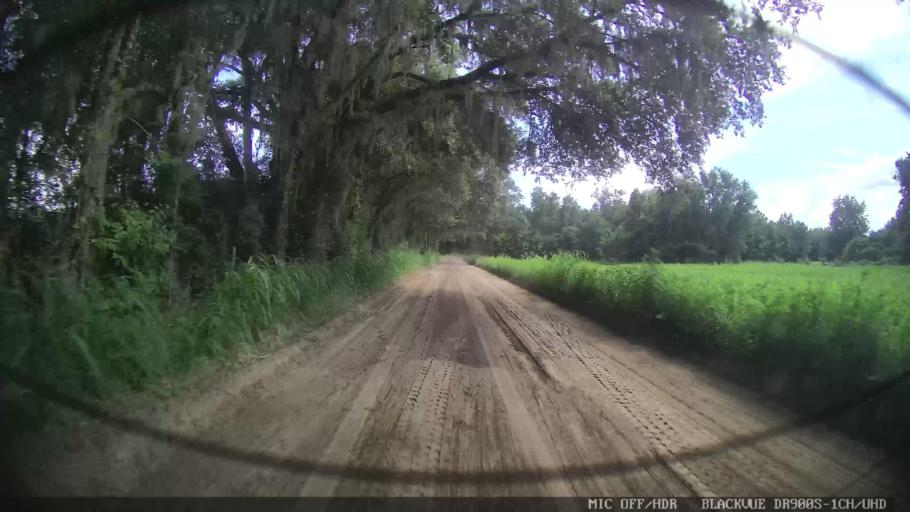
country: US
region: Florida
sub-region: Madison County
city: Madison
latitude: 30.5826
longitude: -83.2206
